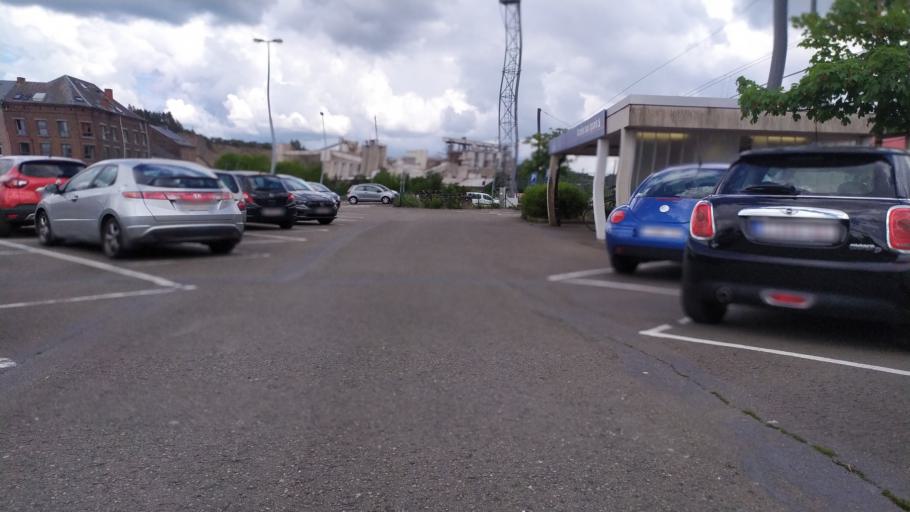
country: BE
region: Wallonia
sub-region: Province de Namur
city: Rochefort
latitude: 50.1602
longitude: 5.2660
